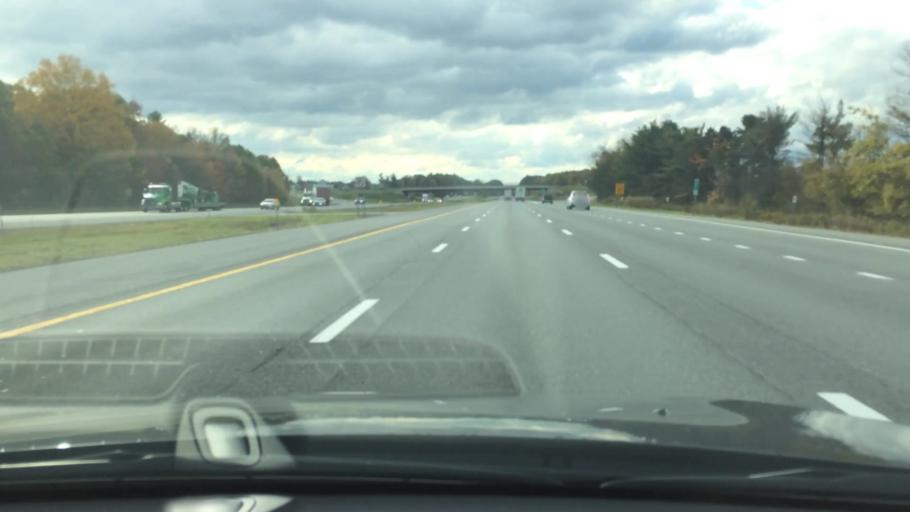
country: US
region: New York
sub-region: Saratoga County
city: Ballston Spa
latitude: 42.9748
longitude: -73.8026
